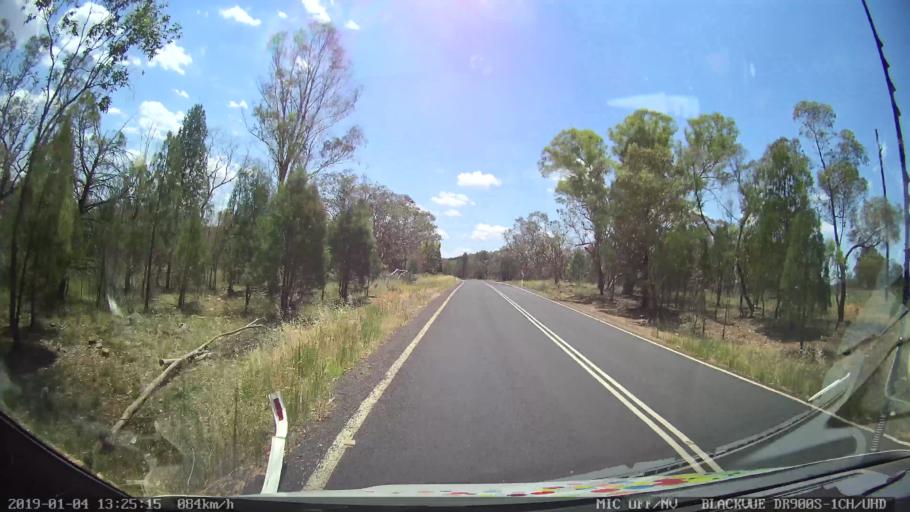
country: AU
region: New South Wales
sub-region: Parkes
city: Peak Hill
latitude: -32.6955
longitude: 148.5552
